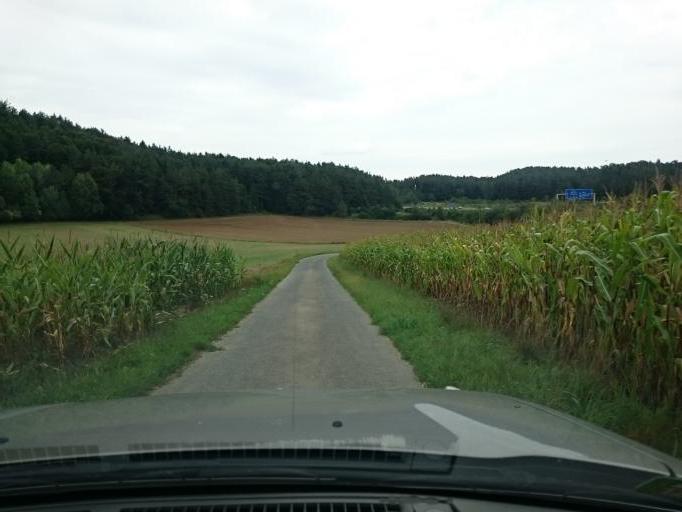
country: DE
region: Bavaria
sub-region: Regierungsbezirk Mittelfranken
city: Velden
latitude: 49.6596
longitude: 11.4597
